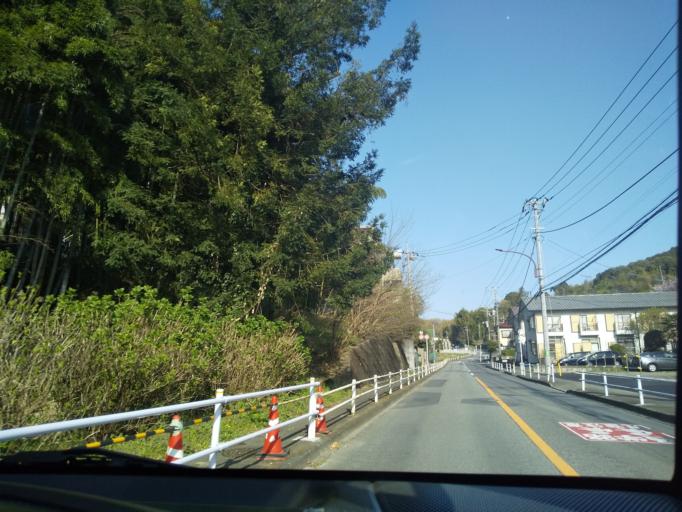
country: JP
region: Tokyo
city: Hino
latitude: 35.6434
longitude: 139.4258
